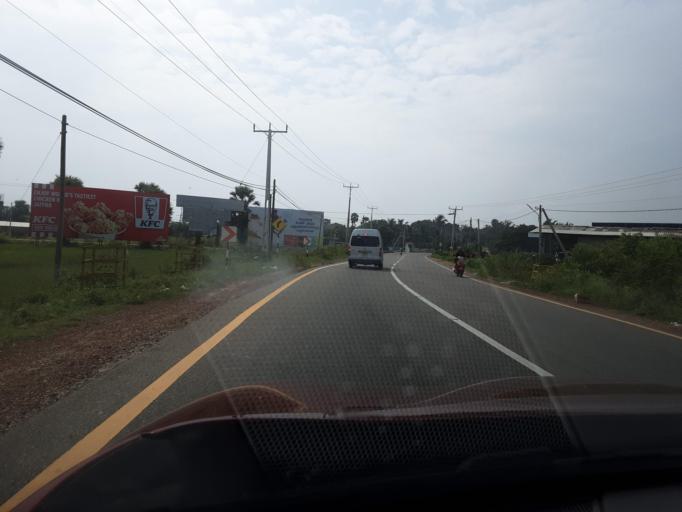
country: LK
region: Northern Province
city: Jaffna
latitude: 9.6605
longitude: 80.0586
